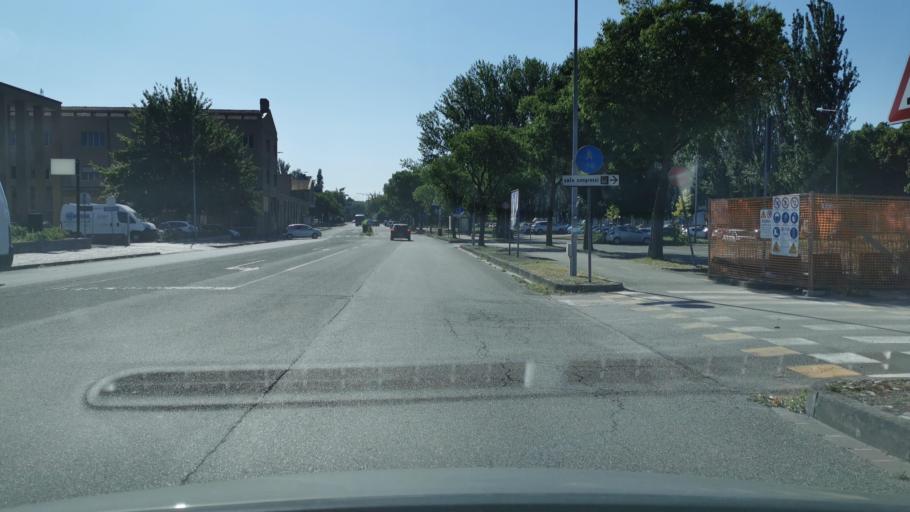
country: IT
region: Emilia-Romagna
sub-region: Provincia di Modena
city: Carpi Centro
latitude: 44.7826
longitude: 10.8764
